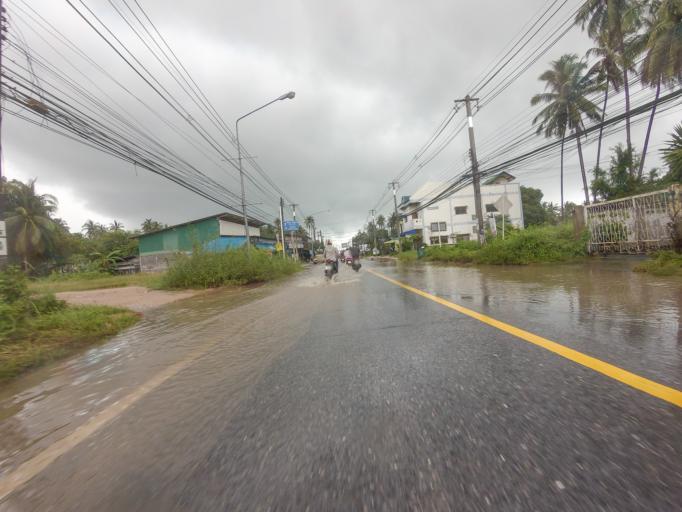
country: TH
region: Surat Thani
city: Ko Samui
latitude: 9.4434
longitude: 100.0198
